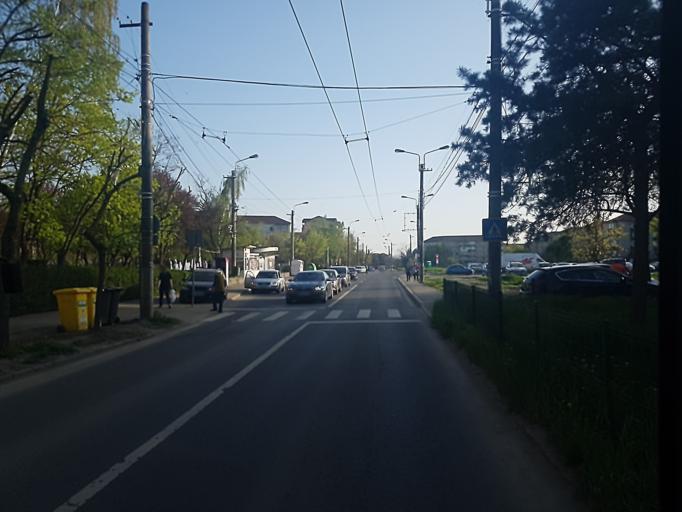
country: RO
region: Timis
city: Timisoara
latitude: 45.7348
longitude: 21.2491
